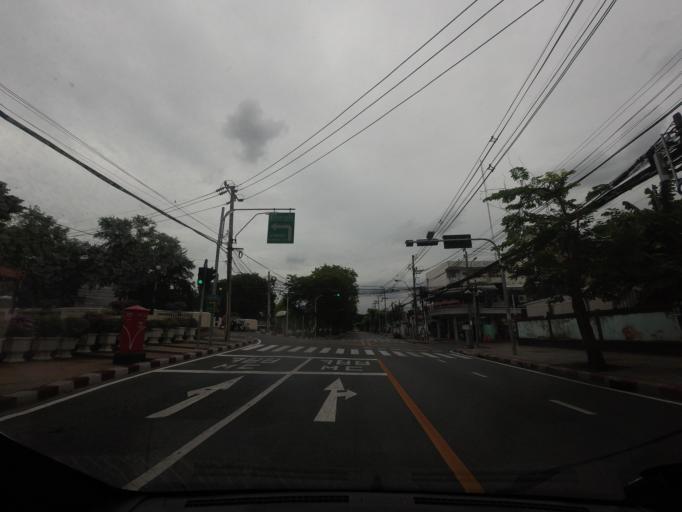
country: TH
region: Bangkok
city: Dusit
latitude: 13.7892
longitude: 100.5275
